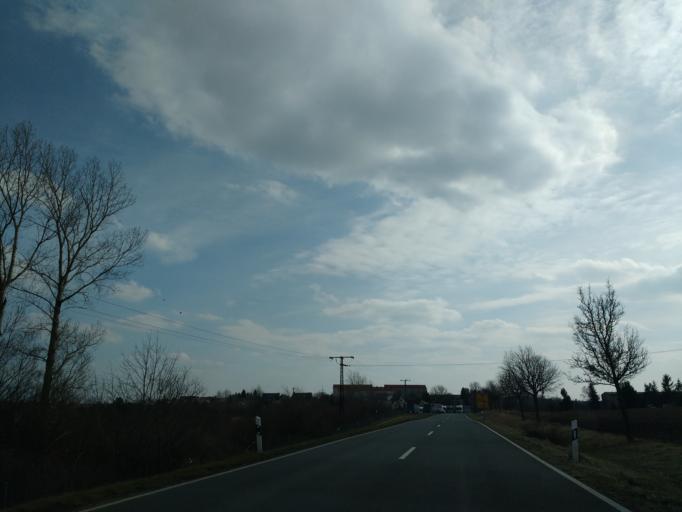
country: DE
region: Saxony-Anhalt
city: Schraplau
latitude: 51.4385
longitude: 11.6569
